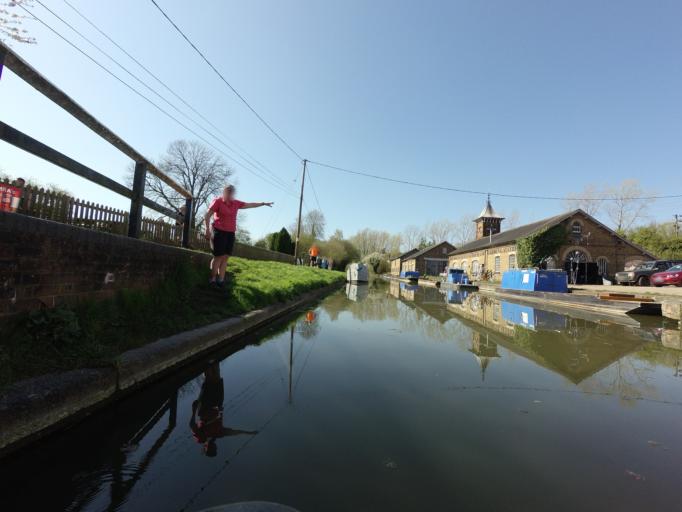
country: GB
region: England
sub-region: Hertfordshire
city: Tring
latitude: 51.8139
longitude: -0.6480
